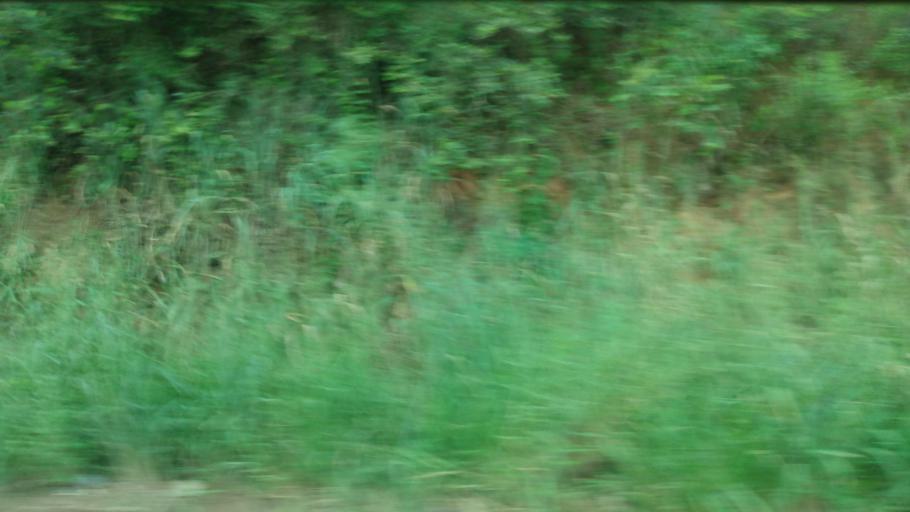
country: BR
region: Pernambuco
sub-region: Maraial
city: Maraial
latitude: -8.7285
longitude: -35.7904
